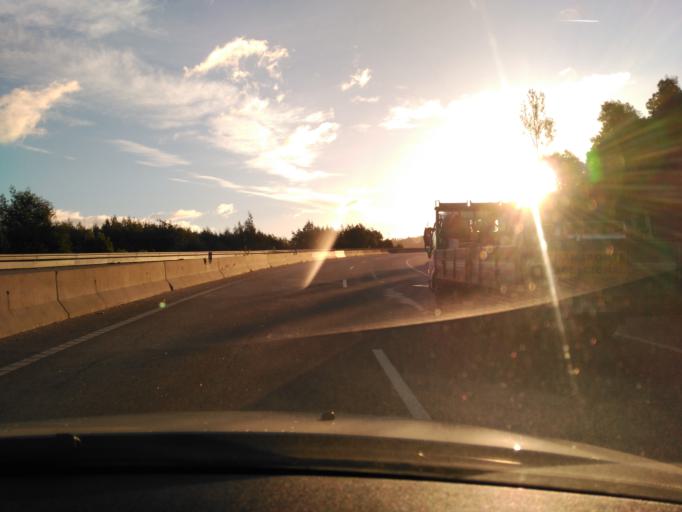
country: PT
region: Braga
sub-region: Guimaraes
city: Guimaraes
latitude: 41.4564
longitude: -8.2659
